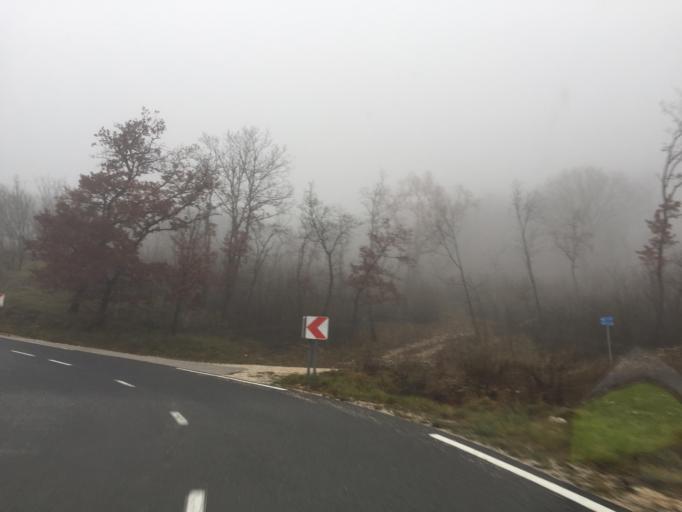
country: SI
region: Ajdovscina
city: Lokavec
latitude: 45.9218
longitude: 13.8971
